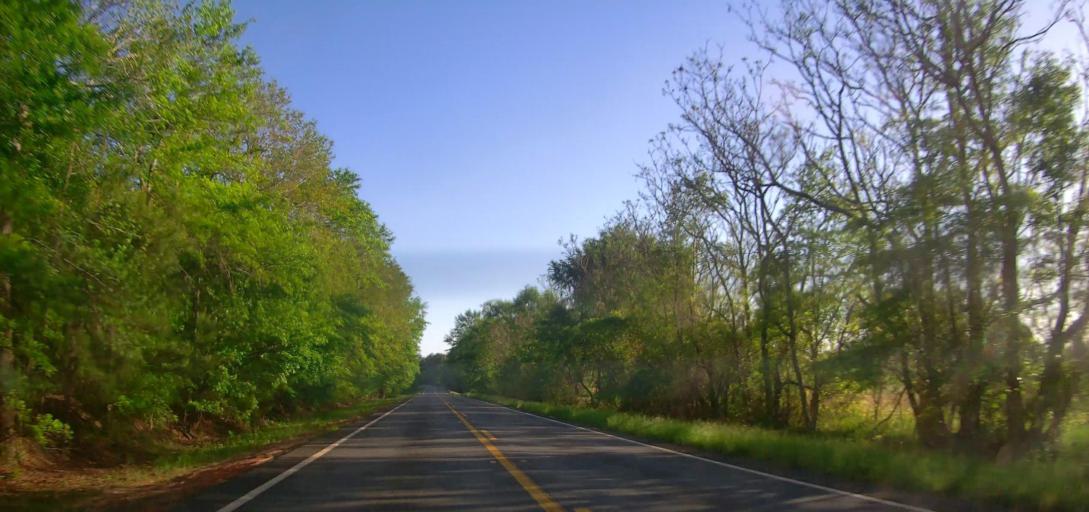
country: US
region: Georgia
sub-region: Macon County
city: Oglethorpe
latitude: 32.2896
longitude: -84.1566
